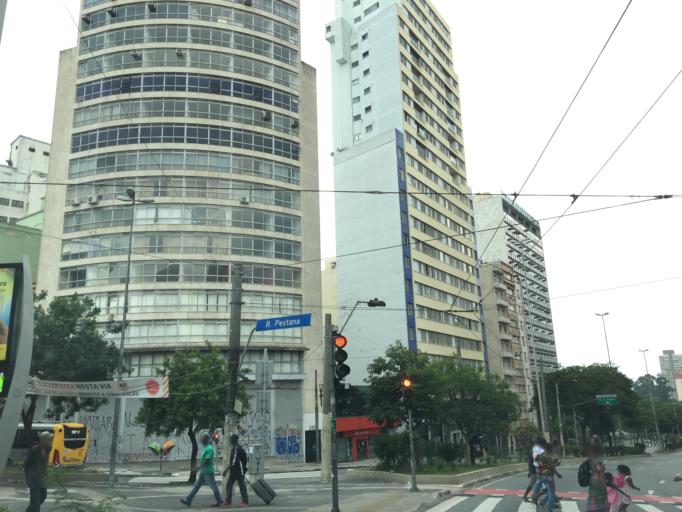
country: BR
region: Sao Paulo
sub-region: Sao Paulo
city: Sao Paulo
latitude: -23.5505
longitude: -46.6318
